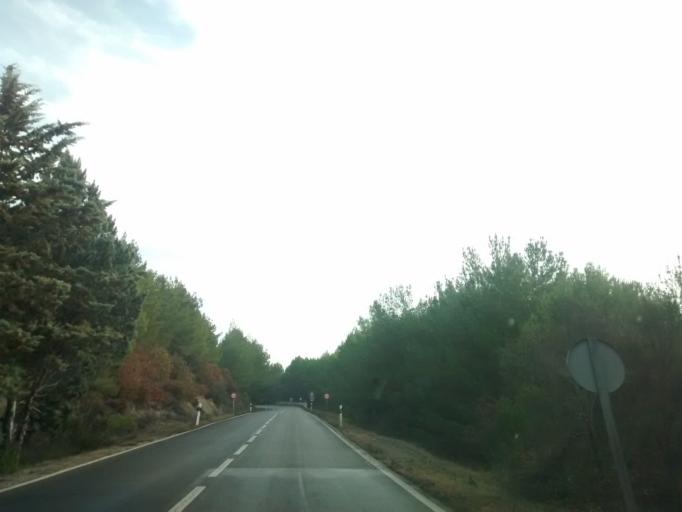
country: ES
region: Aragon
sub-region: Provincia de Zaragoza
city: Siguees
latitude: 42.6083
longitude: -1.0934
